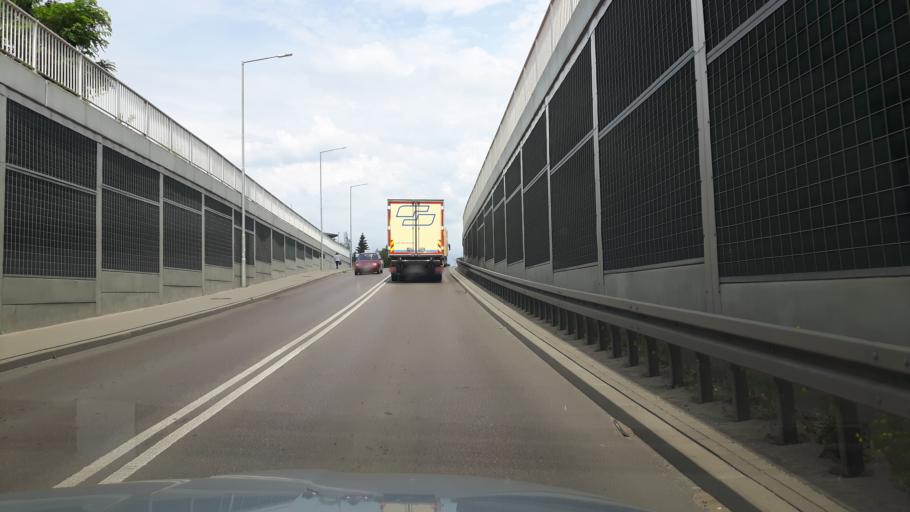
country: PL
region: Masovian Voivodeship
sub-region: Powiat wolominski
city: Nowe Lipiny
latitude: 52.3552
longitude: 21.2569
